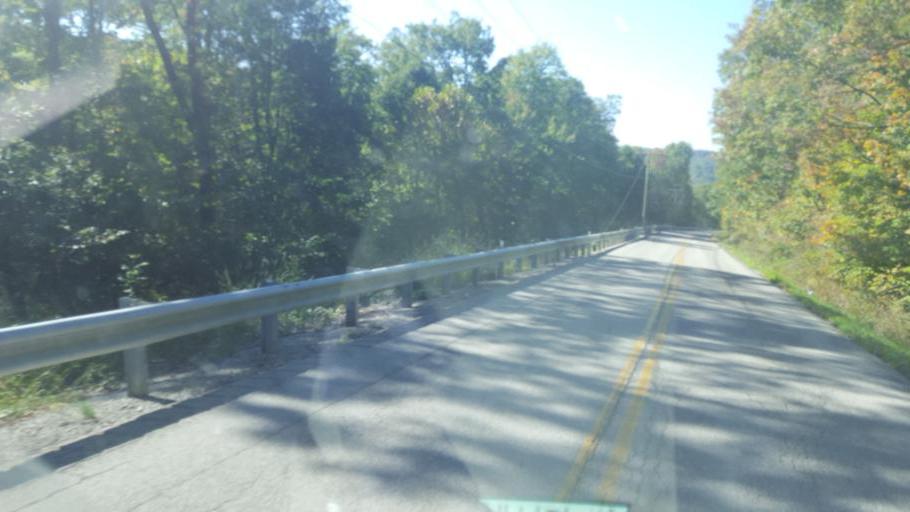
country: US
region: Kentucky
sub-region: Fleming County
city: Flemingsburg
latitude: 38.4629
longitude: -83.5307
